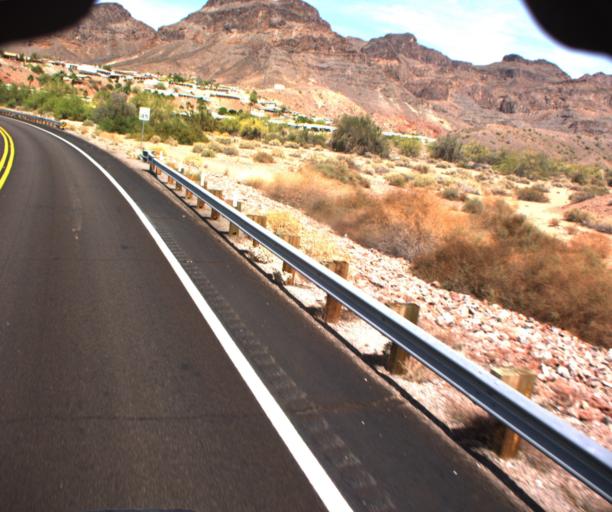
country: US
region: Arizona
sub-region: La Paz County
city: Cienega Springs
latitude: 34.2583
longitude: -114.1302
